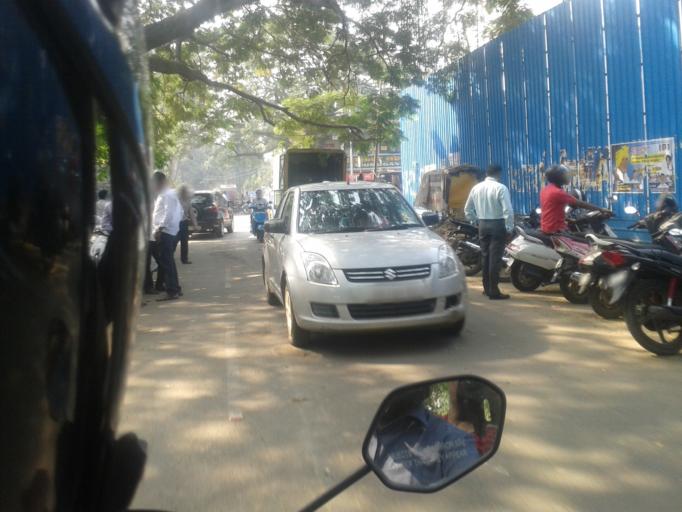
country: IN
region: Tamil Nadu
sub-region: Chennai
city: Chetput
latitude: 13.0830
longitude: 80.2081
